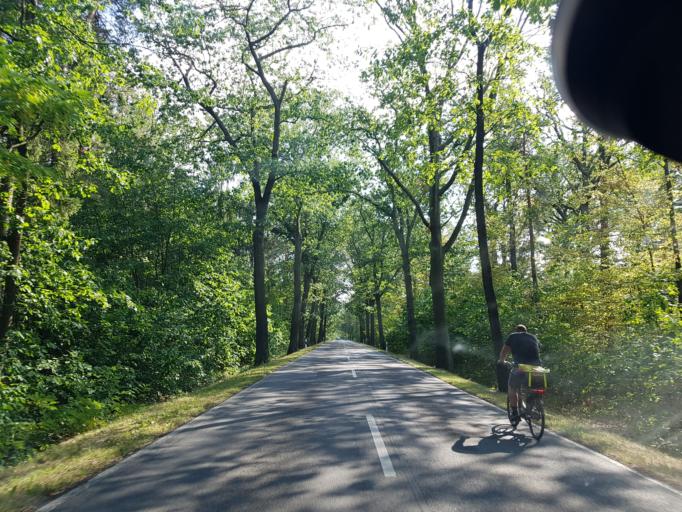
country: DE
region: Brandenburg
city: Calau
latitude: 51.7717
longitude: 13.9514
